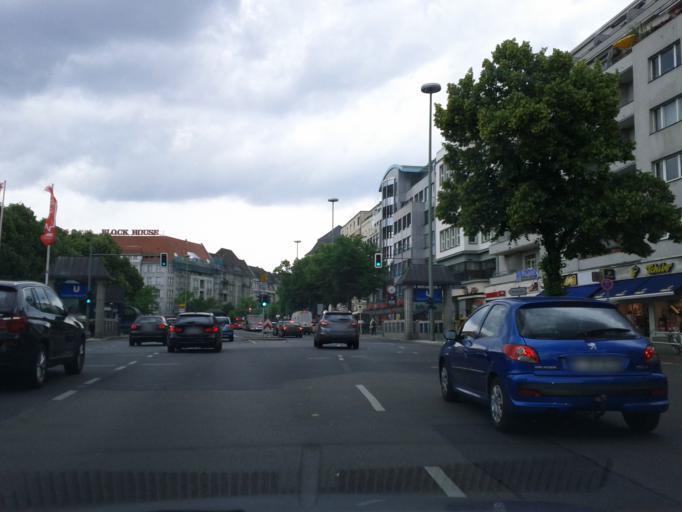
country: DE
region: Berlin
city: Westend
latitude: 52.5097
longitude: 13.2741
